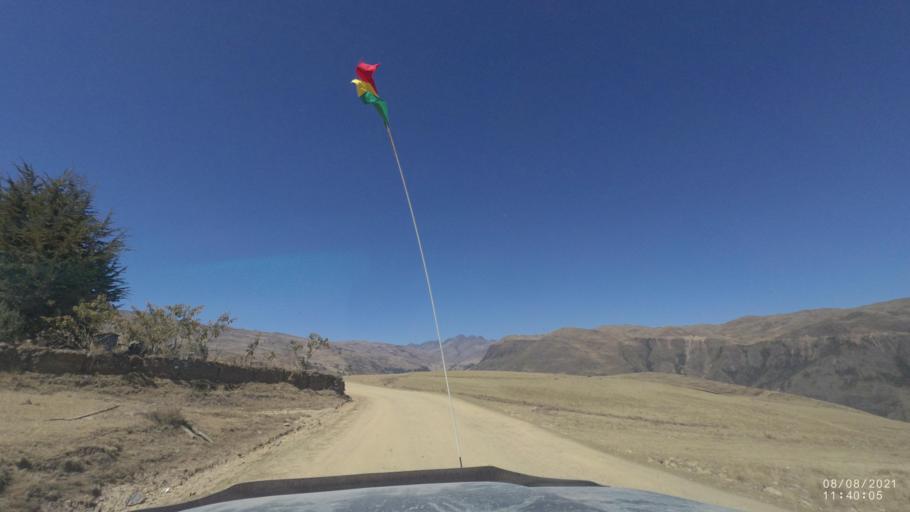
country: BO
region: Cochabamba
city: Colchani
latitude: -16.7967
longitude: -66.6499
